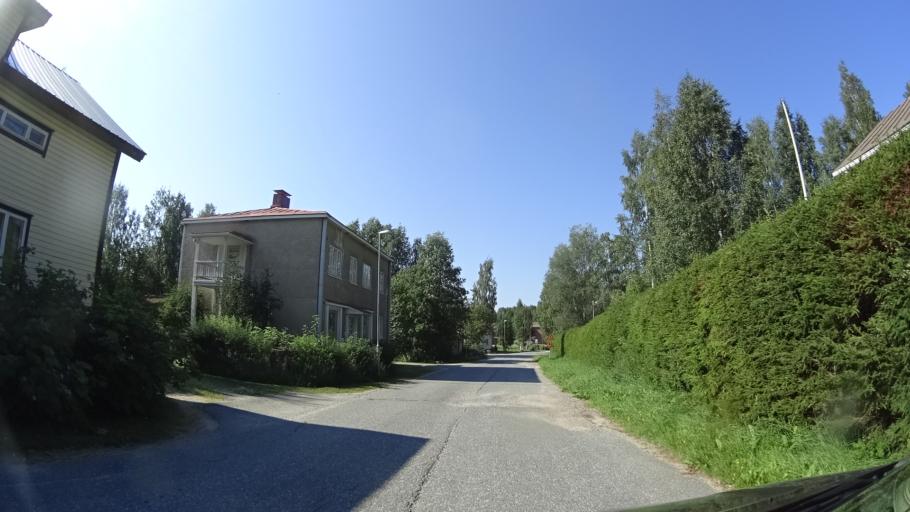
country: FI
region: North Karelia
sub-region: Joensuu
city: Juuka
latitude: 63.2404
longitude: 29.2501
